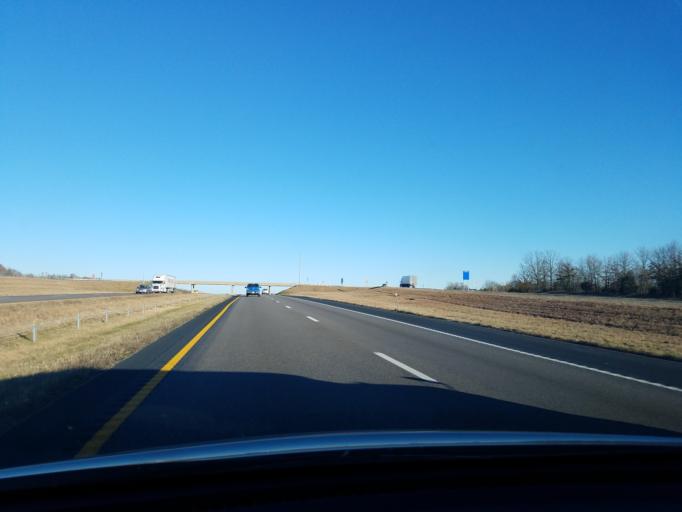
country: US
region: Missouri
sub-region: Crawford County
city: Cuba
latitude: 38.0440
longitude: -91.4900
